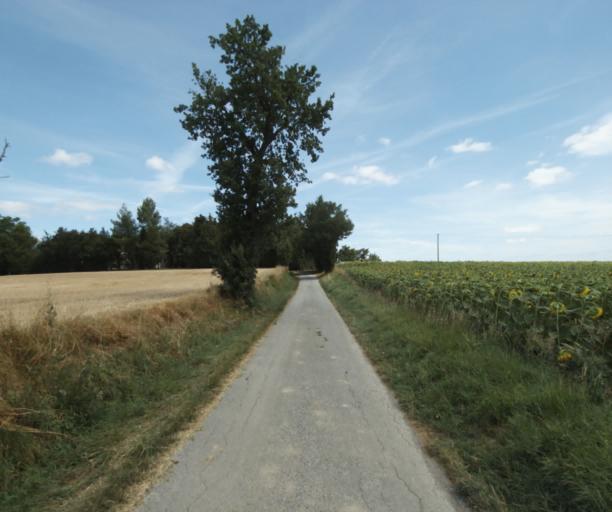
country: FR
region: Midi-Pyrenees
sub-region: Departement du Tarn
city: Soreze
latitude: 43.4872
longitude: 2.0710
